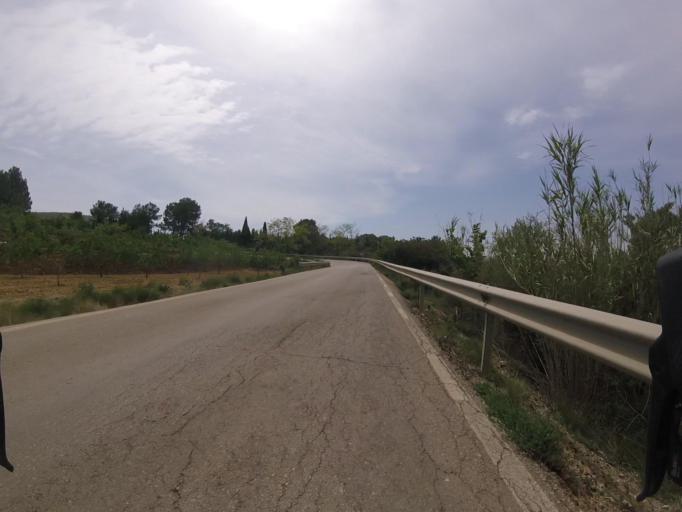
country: ES
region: Valencia
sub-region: Provincia de Castello
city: Cabanes
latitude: 40.1531
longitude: 0.0519
